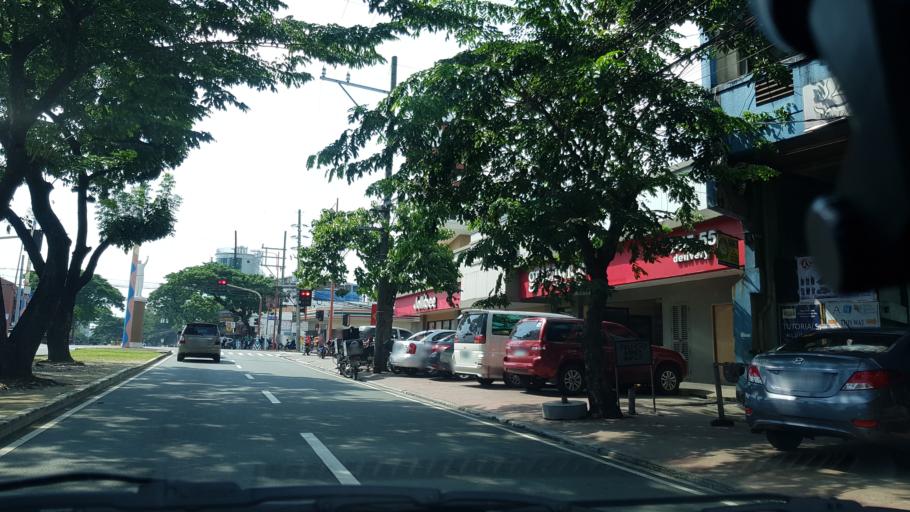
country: PH
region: Calabarzon
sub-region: Province of Rizal
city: Antipolo
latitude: 14.6506
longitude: 121.1125
